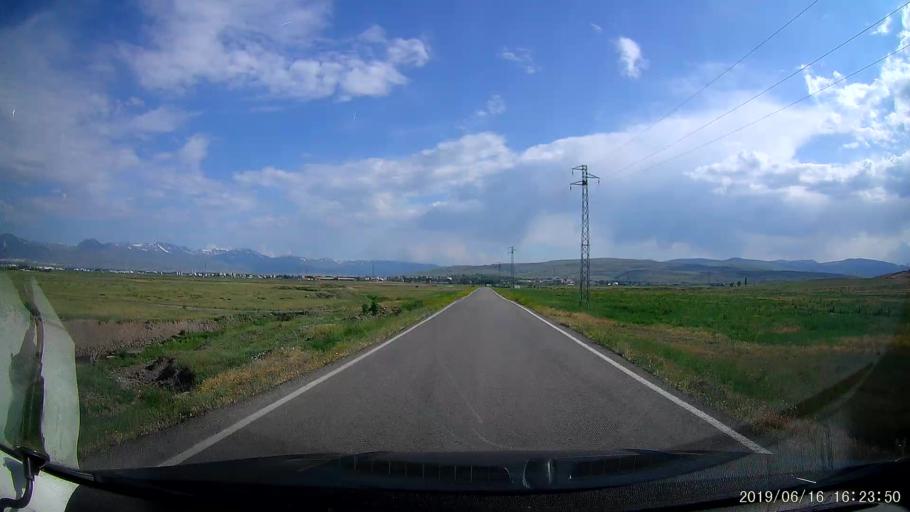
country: TR
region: Erzurum
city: Ilica
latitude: 39.9736
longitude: 41.1053
